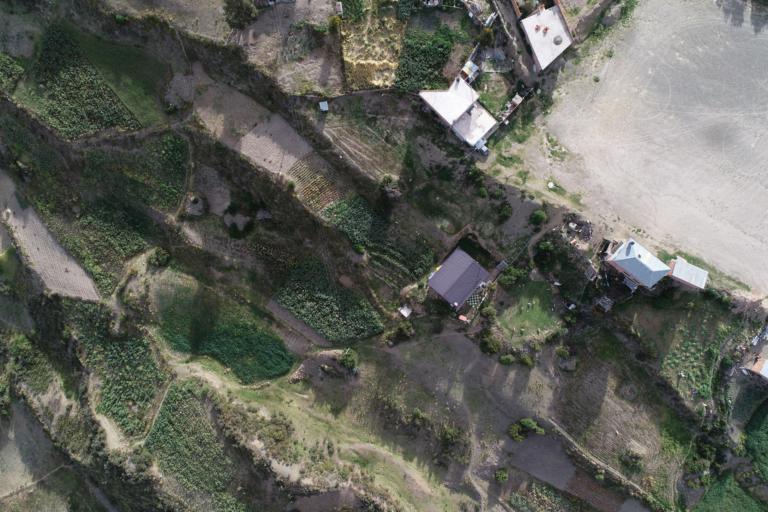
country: BO
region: La Paz
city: La Paz
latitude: -16.5472
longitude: -67.9988
